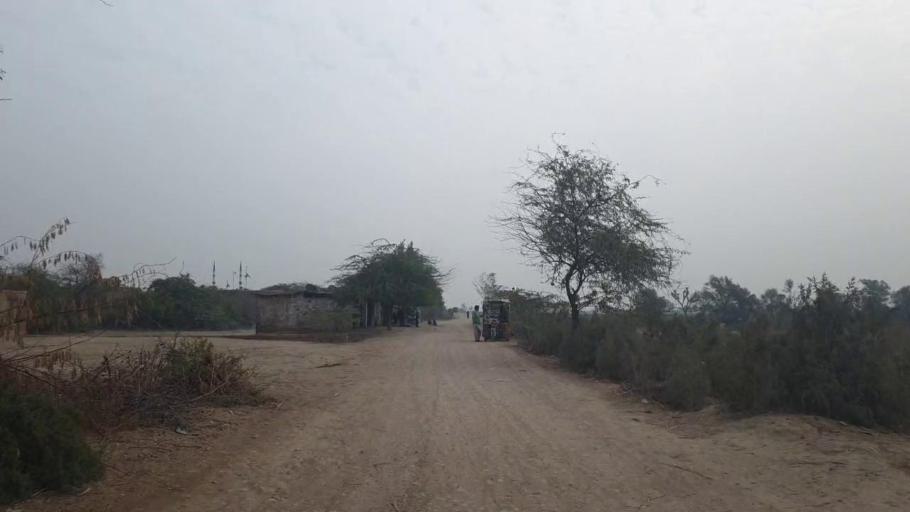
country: PK
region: Sindh
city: Tando Adam
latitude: 25.7272
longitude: 68.7185
